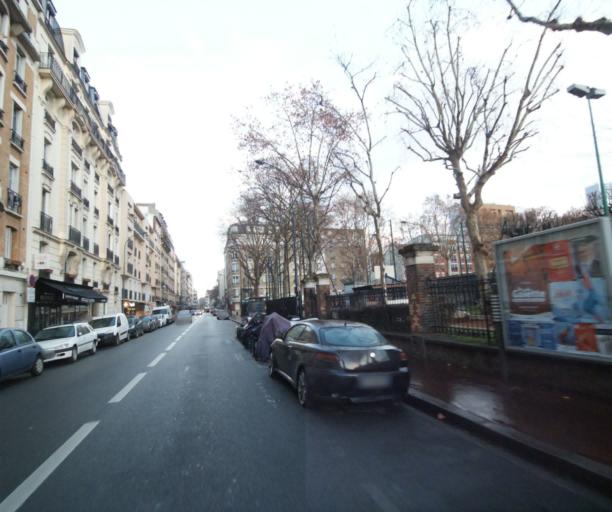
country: FR
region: Ile-de-France
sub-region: Departement des Hauts-de-Seine
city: Clichy
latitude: 48.8979
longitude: 2.3013
